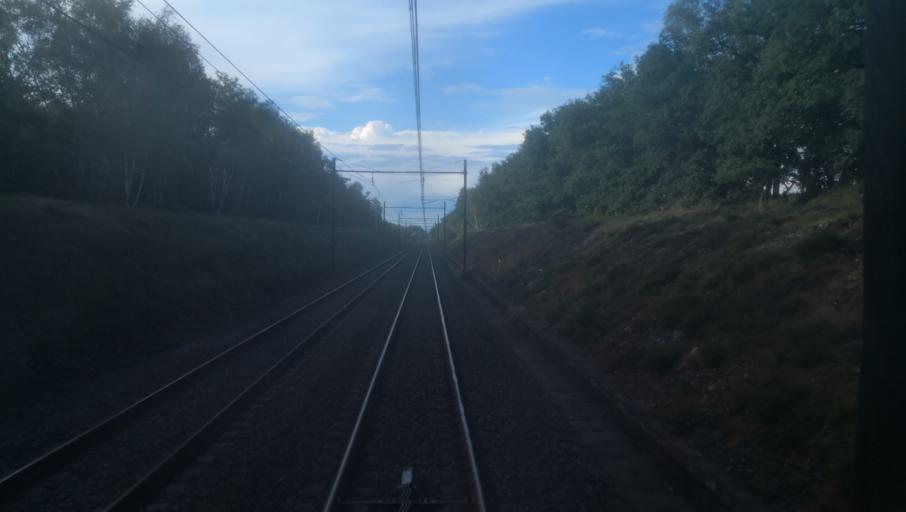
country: FR
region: Centre
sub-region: Departement du Loir-et-Cher
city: Theillay
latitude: 47.3593
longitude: 2.0480
